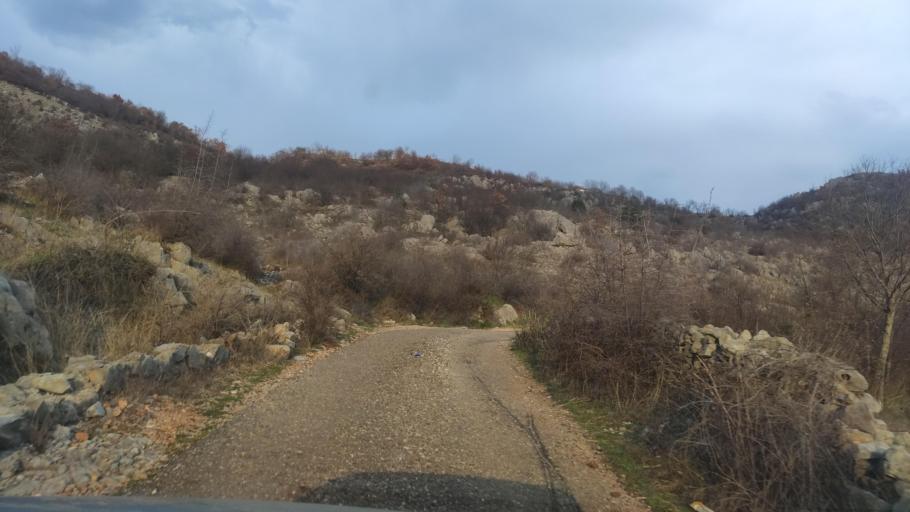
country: AL
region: Shkoder
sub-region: Rrethi i Malesia e Madhe
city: Gruemire
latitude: 42.2392
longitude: 19.5347
